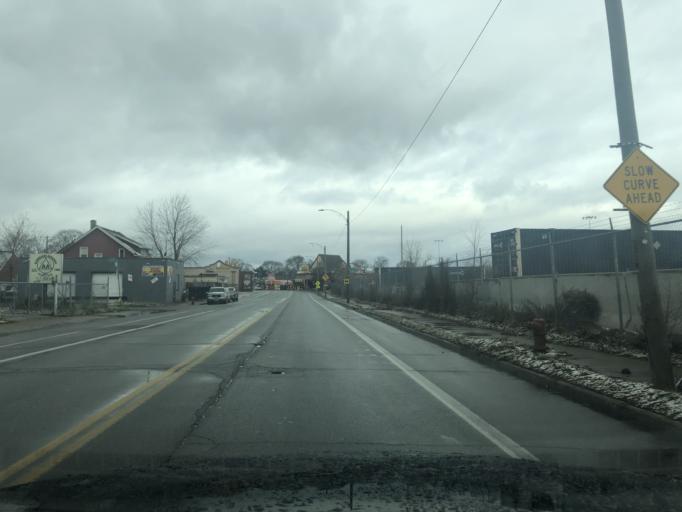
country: US
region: Michigan
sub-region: Wayne County
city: River Rouge
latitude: 42.3166
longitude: -83.1220
